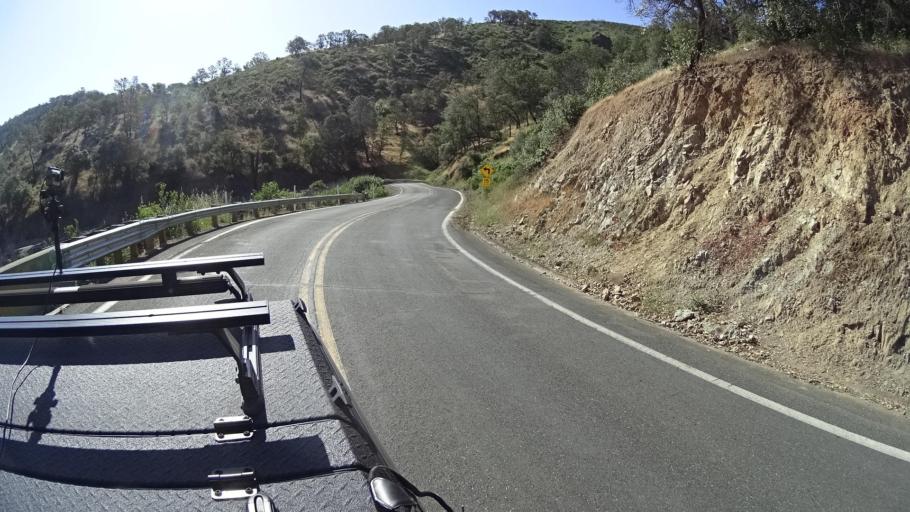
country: US
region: California
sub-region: Lake County
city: Clearlake Oaks
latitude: 38.9981
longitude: -122.6625
